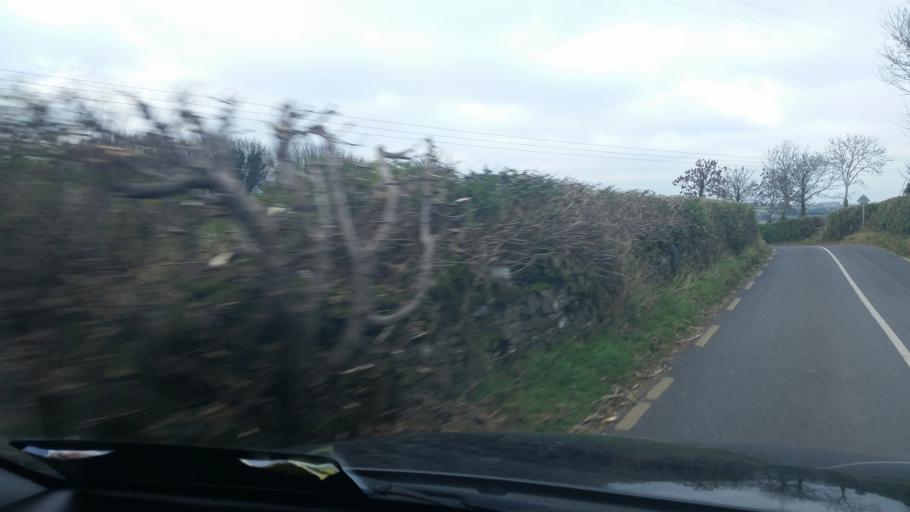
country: IE
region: Leinster
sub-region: Lu
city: Tullyallen
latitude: 53.7154
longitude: -6.4102
